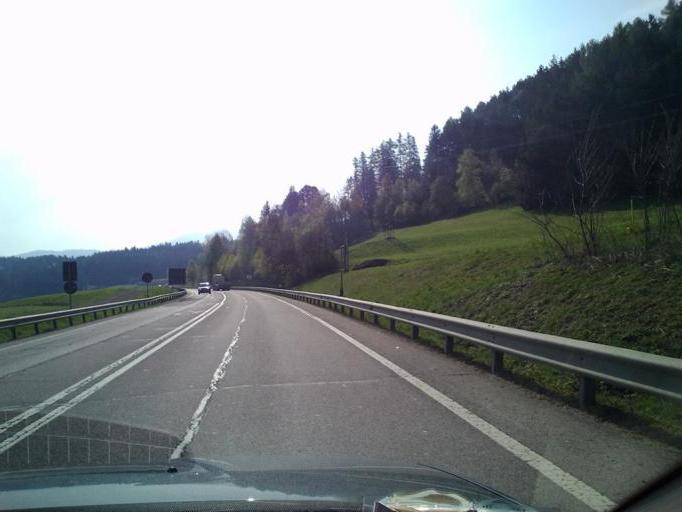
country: IT
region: Trentino-Alto Adige
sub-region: Bolzano
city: San Lorenzo di Sebato
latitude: 46.7818
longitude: 11.9118
